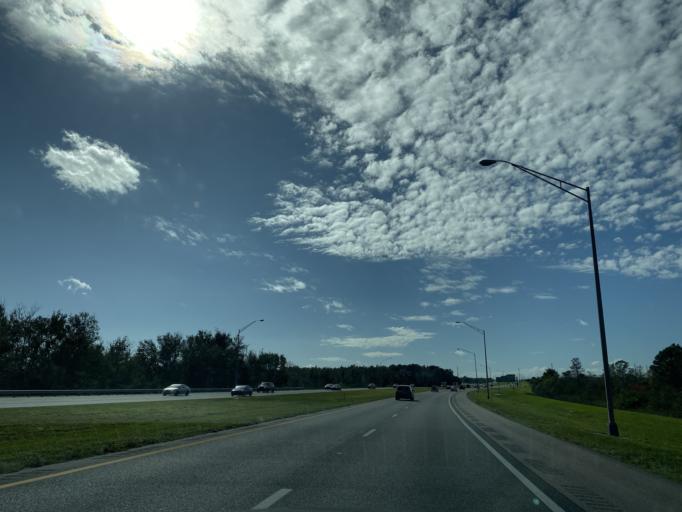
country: US
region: Florida
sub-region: Orange County
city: Taft
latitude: 28.4069
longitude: -81.2333
